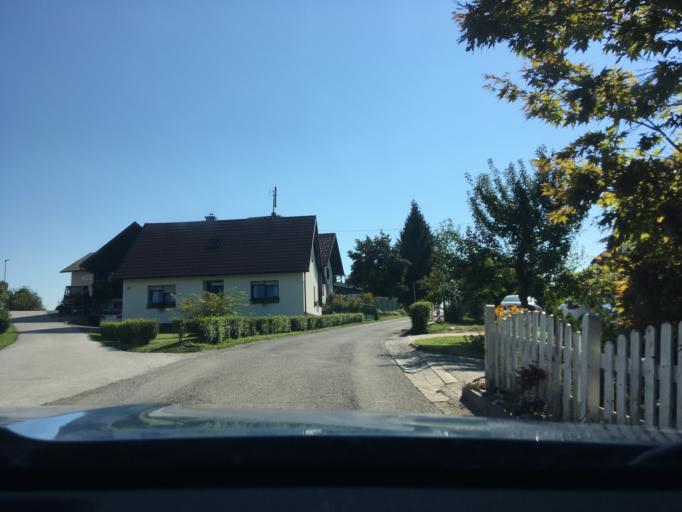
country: SI
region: Crnomelj
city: Crnomelj
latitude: 45.4604
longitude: 15.2524
